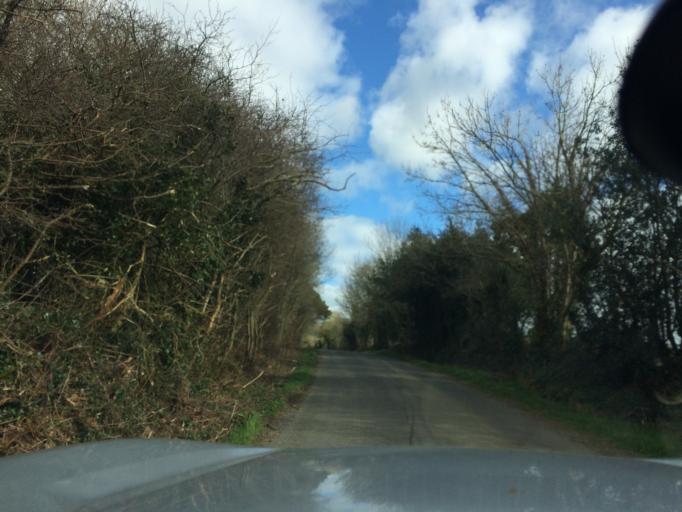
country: IE
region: Munster
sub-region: Waterford
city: Portlaw
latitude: 52.2774
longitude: -7.3661
